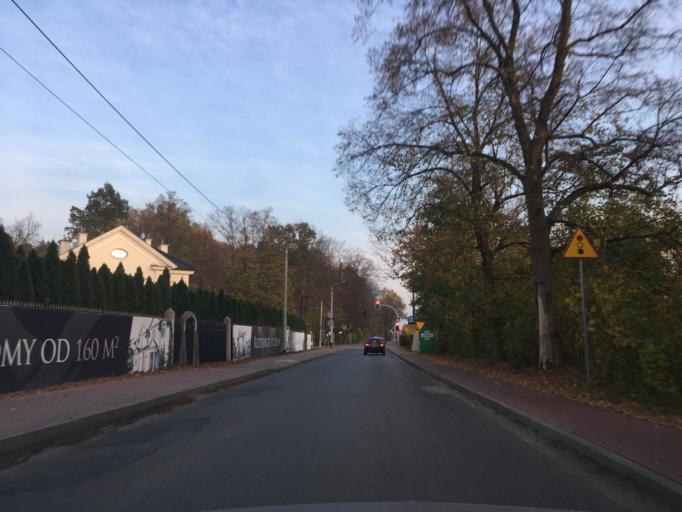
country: PL
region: Masovian Voivodeship
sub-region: Powiat pruszkowski
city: Nadarzyn
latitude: 52.0923
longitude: 20.8443
